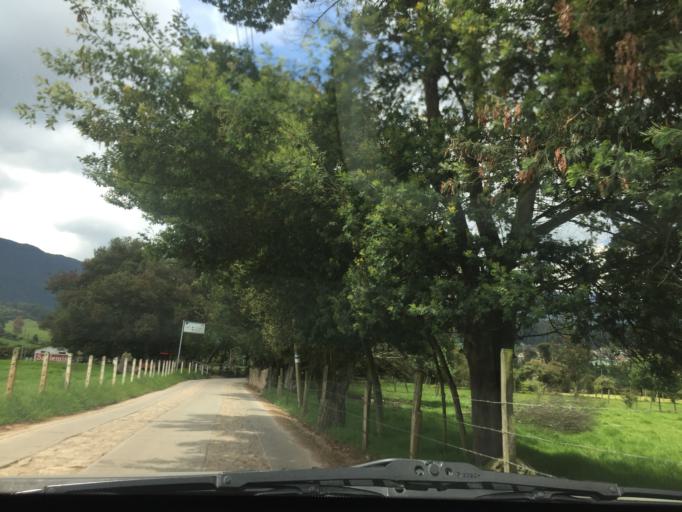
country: CO
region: Cundinamarca
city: Cogua
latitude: 5.0534
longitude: -73.9936
